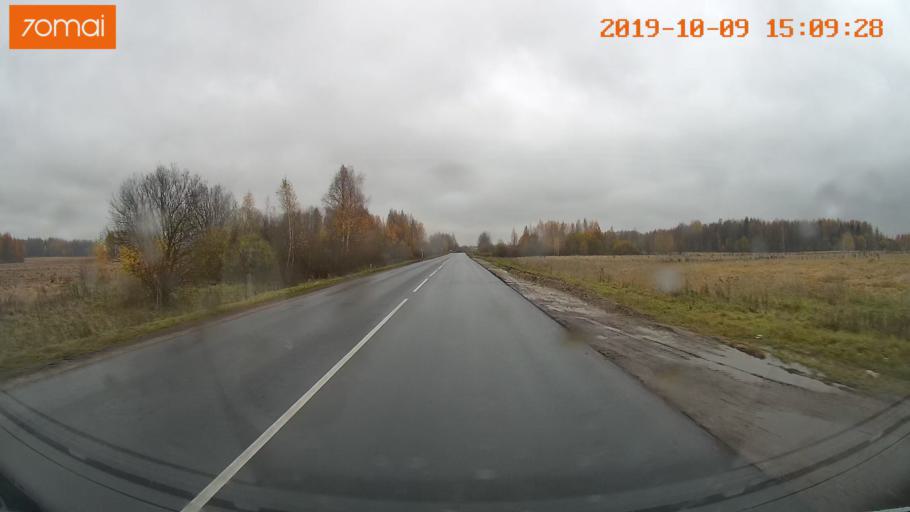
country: RU
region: Kostroma
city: Susanino
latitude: 58.1910
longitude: 41.6501
